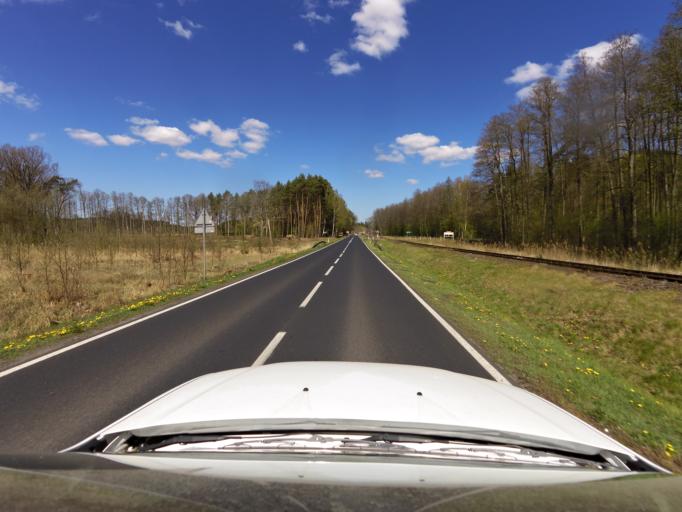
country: PL
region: West Pomeranian Voivodeship
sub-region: Powiat mysliborski
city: Debno
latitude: 52.7640
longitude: 14.7389
